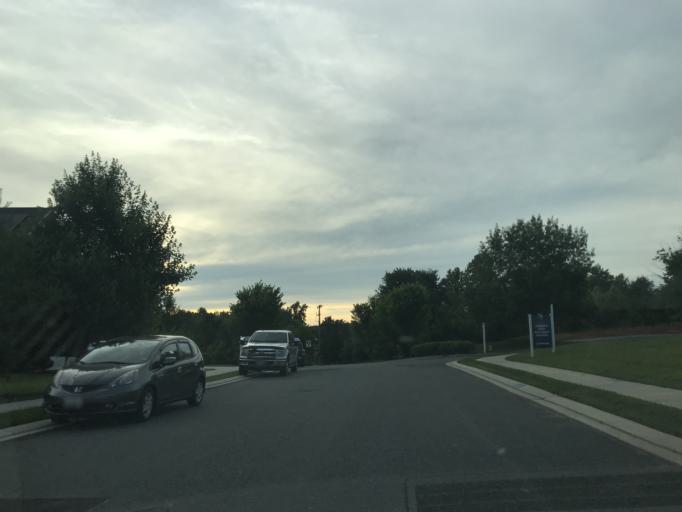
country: US
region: Maryland
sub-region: Harford County
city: Perryman
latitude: 39.5000
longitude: -76.2079
